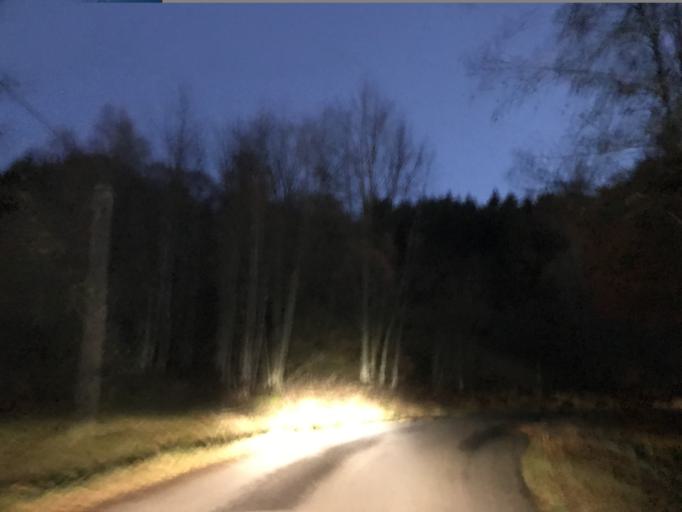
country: FR
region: Rhone-Alpes
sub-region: Departement de la Loire
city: Noiretable
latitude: 45.7409
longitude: 3.7155
